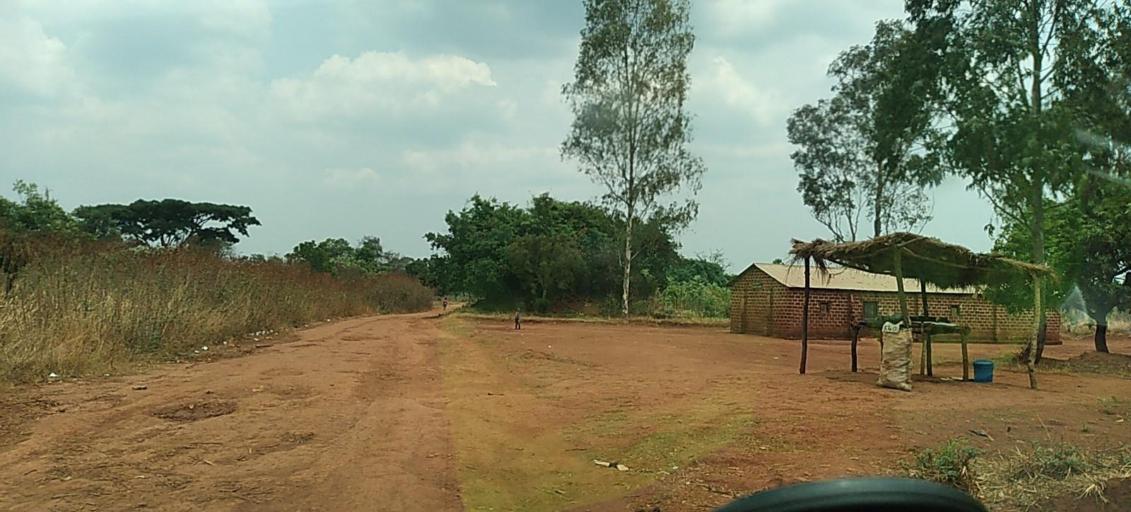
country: ZM
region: North-Western
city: Kansanshi
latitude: -12.0412
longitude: 26.3966
